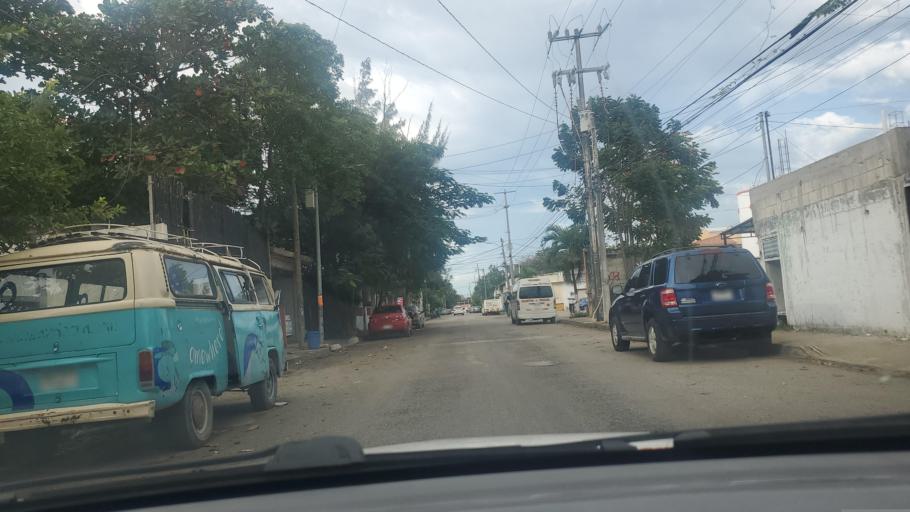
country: MX
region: Quintana Roo
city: Tulum
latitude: 20.2119
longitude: -87.4651
